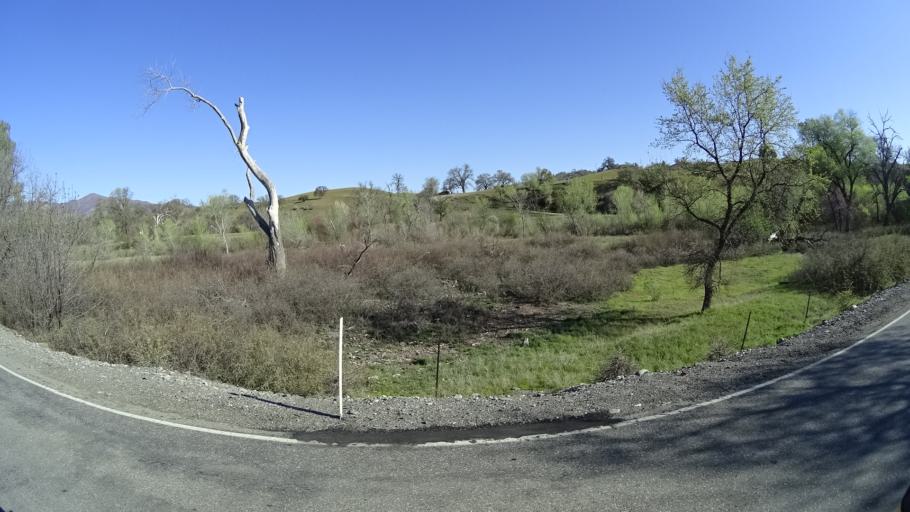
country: US
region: California
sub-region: Glenn County
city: Orland
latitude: 39.6785
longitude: -122.5294
